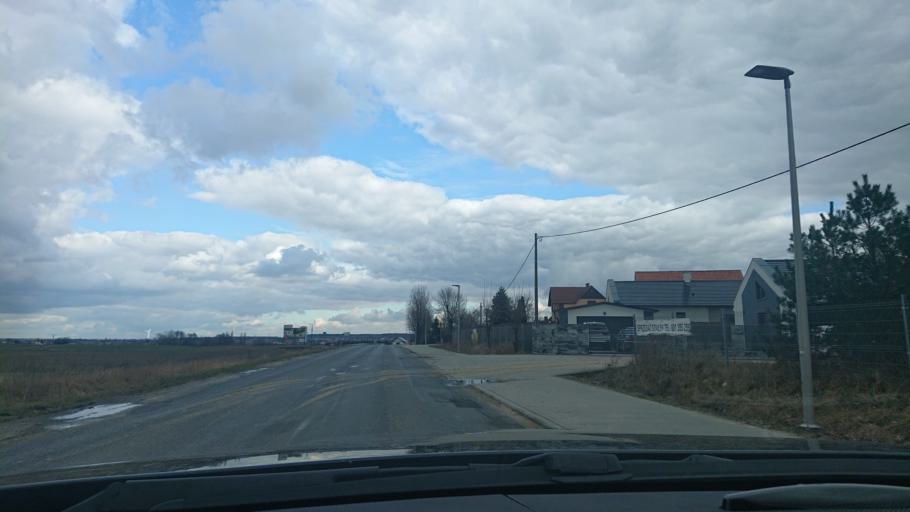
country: PL
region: Greater Poland Voivodeship
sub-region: Powiat gnieznienski
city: Niechanowo
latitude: 52.5486
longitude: 17.6735
